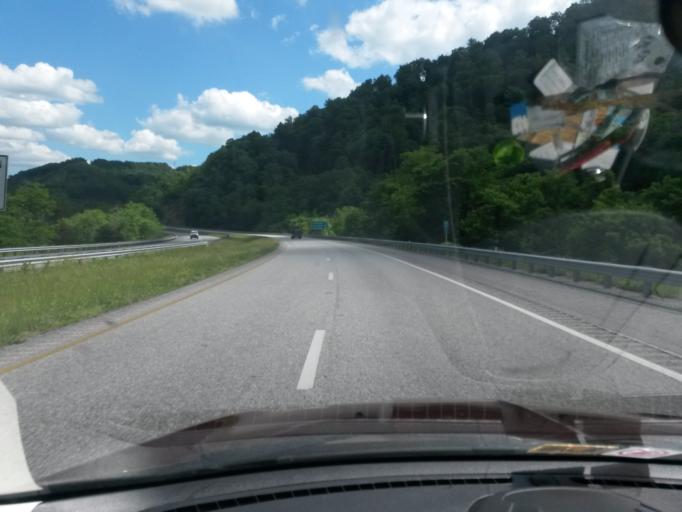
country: US
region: Virginia
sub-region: City of Covington
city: Covington
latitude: 37.8000
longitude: -80.0550
